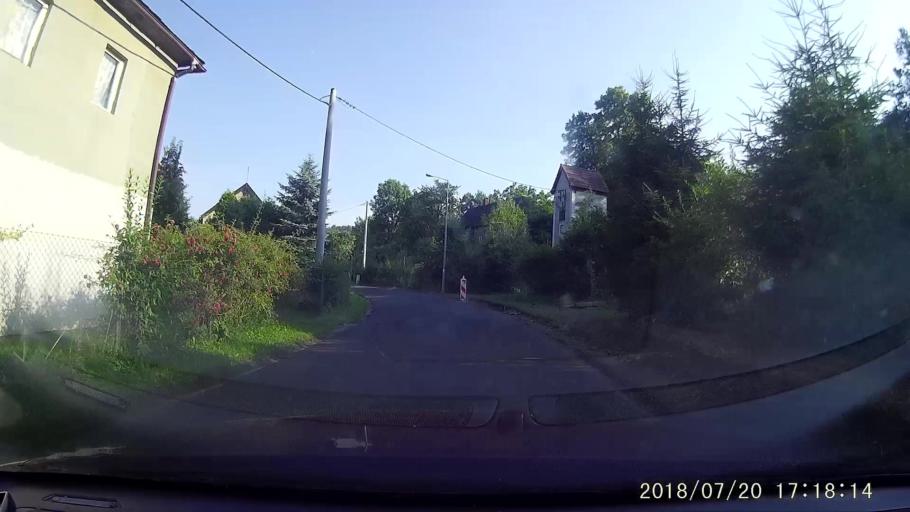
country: PL
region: Lower Silesian Voivodeship
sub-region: Powiat lubanski
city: Lesna
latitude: 50.9953
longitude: 15.2862
